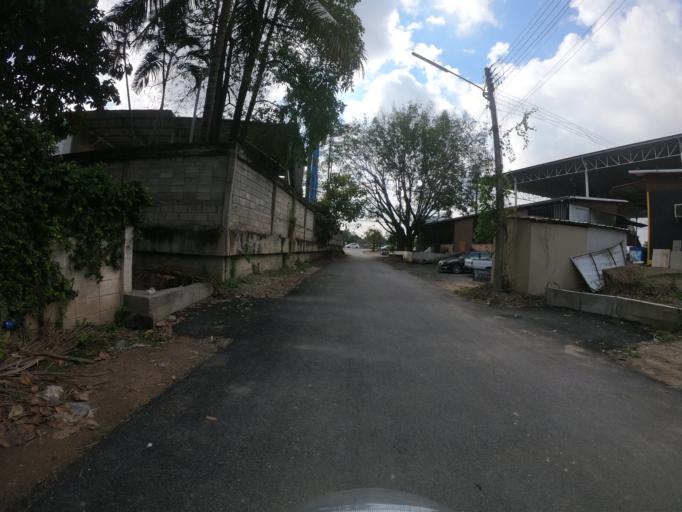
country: TH
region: Chiang Mai
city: Chiang Mai
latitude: 18.8104
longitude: 98.9752
